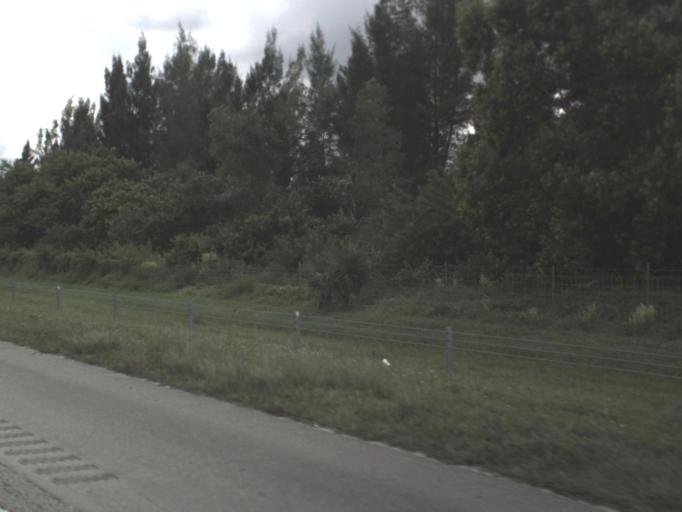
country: US
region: Florida
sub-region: Palm Beach County
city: Plantation Mobile Home Park
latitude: 26.7218
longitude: -80.1357
